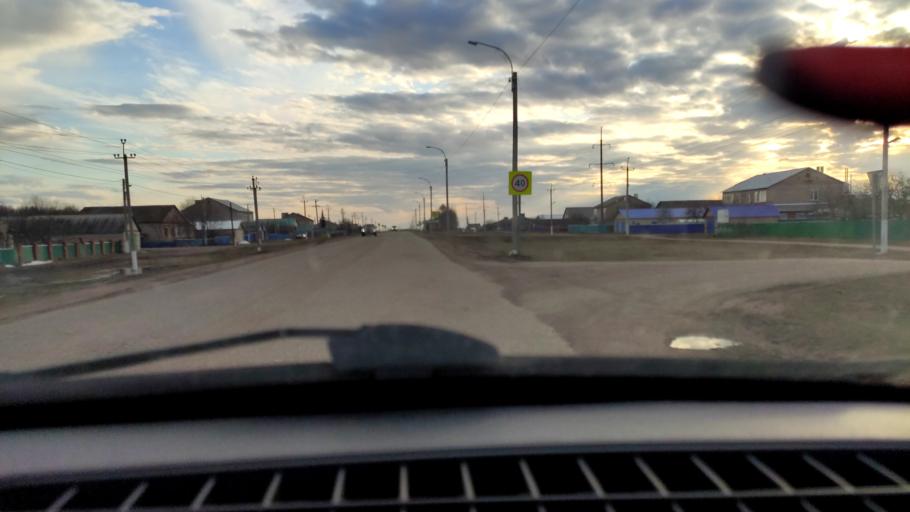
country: RU
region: Bashkortostan
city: Tolbazy
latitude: 54.0063
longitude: 55.8717
